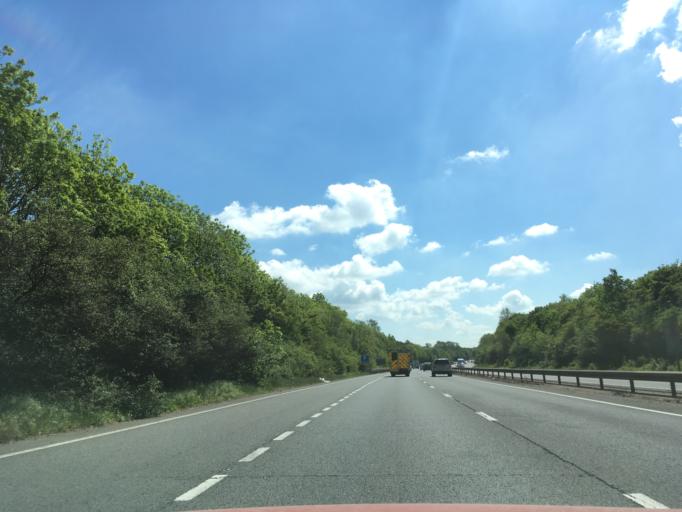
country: GB
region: England
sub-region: Milton Keynes
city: Bradwell
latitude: 52.0452
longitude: -0.7964
